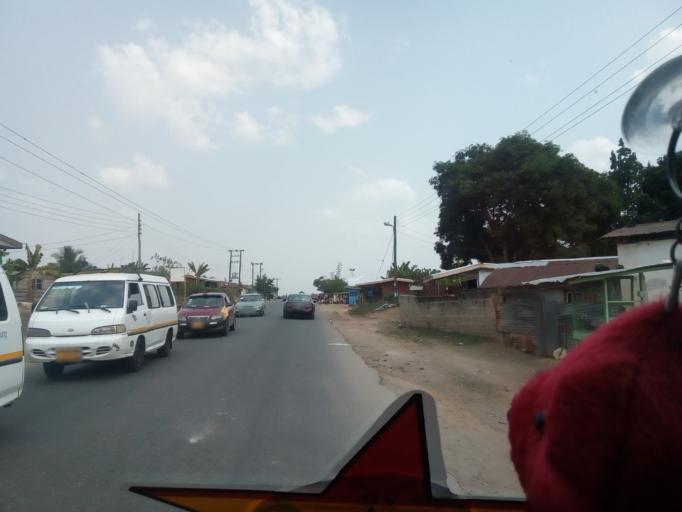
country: GH
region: Eastern
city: Suhum
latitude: 6.0423
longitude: -0.4365
